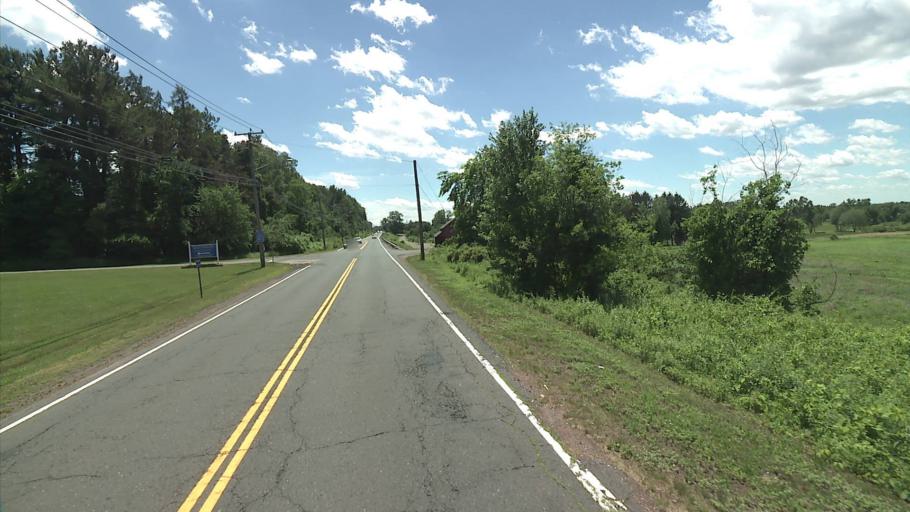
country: US
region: Massachusetts
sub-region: Hampden County
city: East Longmeadow
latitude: 42.0234
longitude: -72.5150
